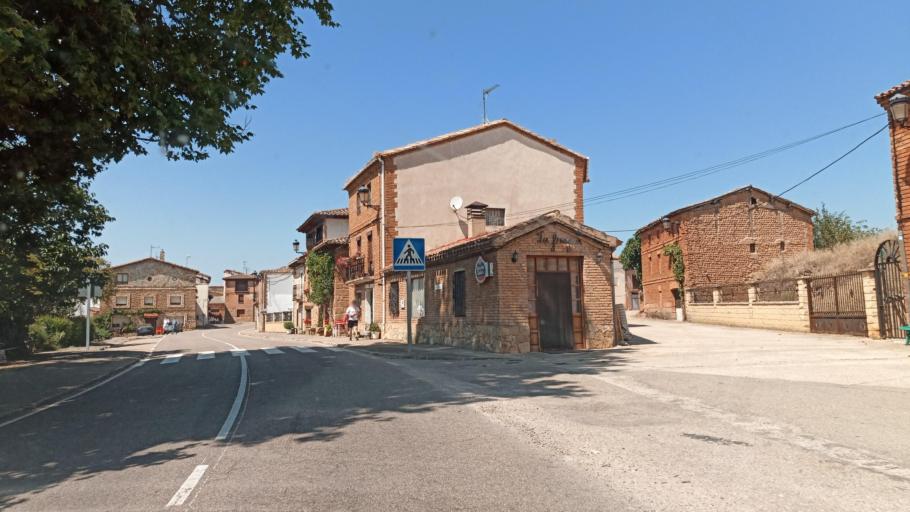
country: ES
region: Castille and Leon
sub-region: Provincia de Burgos
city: Piernigas
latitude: 42.6447
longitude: -3.3889
